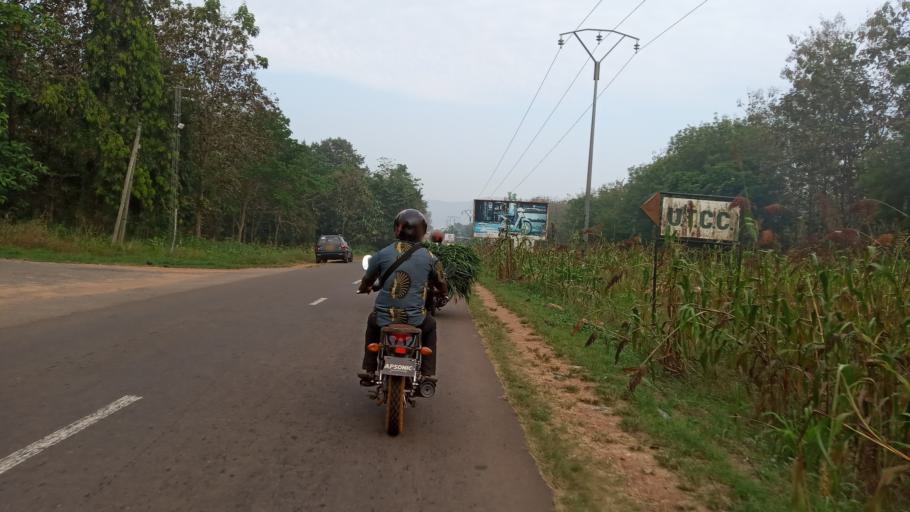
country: TG
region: Plateaux
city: Kpalime
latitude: 6.8875
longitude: 0.6437
